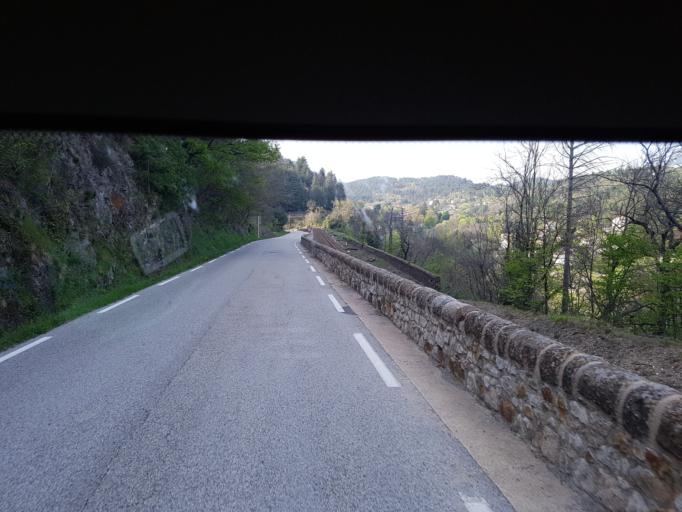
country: FR
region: Languedoc-Roussillon
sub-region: Departement du Gard
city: Branoux-les-Taillades
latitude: 44.3392
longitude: 3.9526
